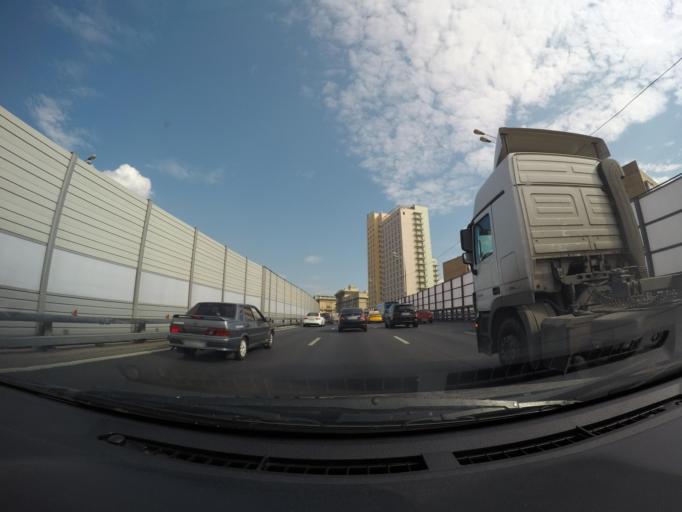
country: RU
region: Moscow
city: Mar'ina Roshcha
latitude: 55.7922
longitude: 37.6299
